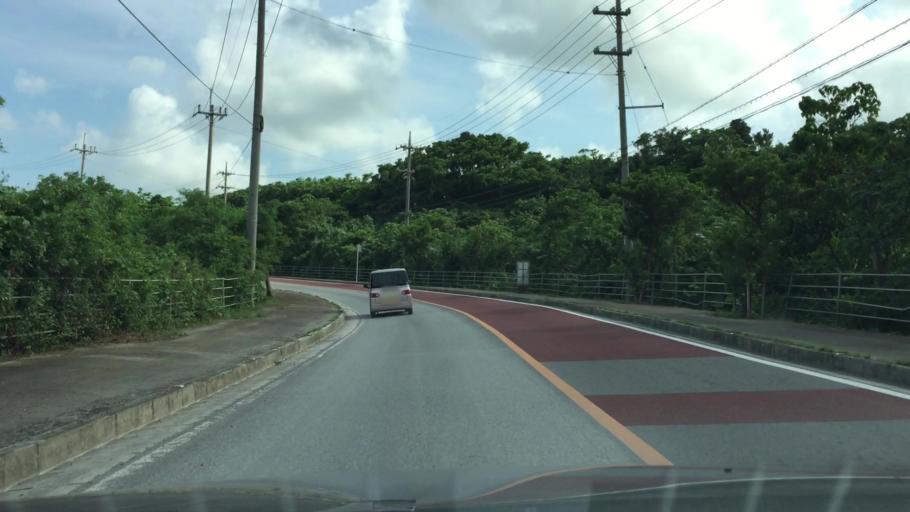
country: JP
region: Okinawa
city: Ishigaki
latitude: 24.4318
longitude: 124.2476
